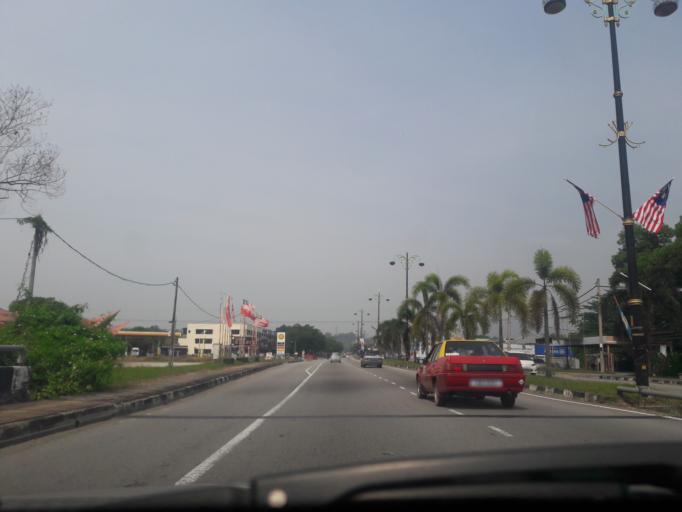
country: MY
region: Kedah
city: Kulim
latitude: 5.3870
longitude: 100.5603
